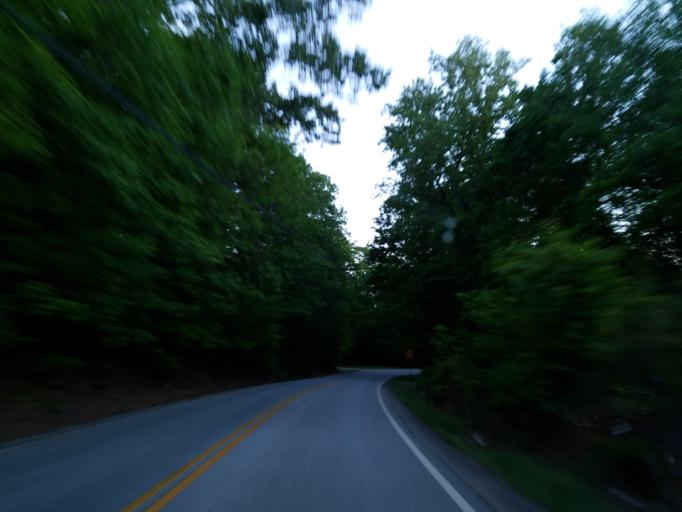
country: US
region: Georgia
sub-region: Lumpkin County
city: Dahlonega
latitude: 34.5916
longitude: -83.9695
